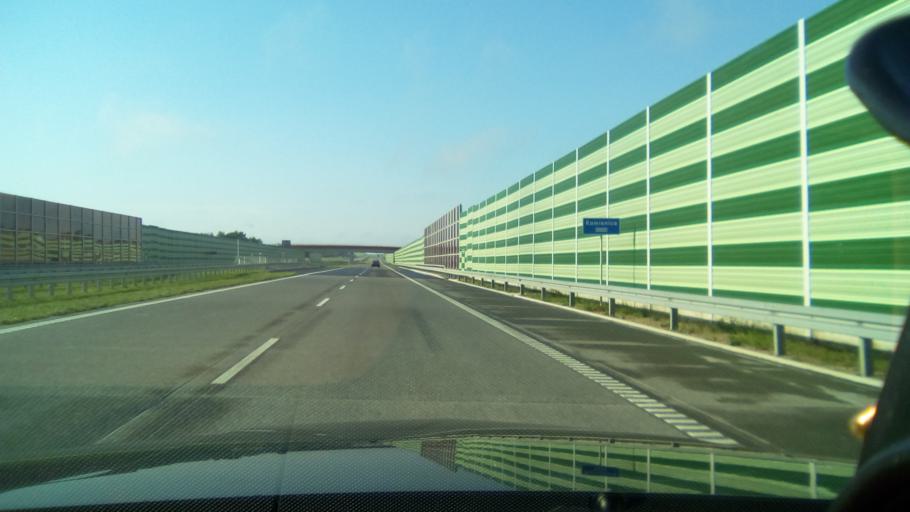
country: PL
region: Silesian Voivodeship
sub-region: Powiat czestochowski
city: Starcza
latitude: 50.6443
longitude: 19.0366
